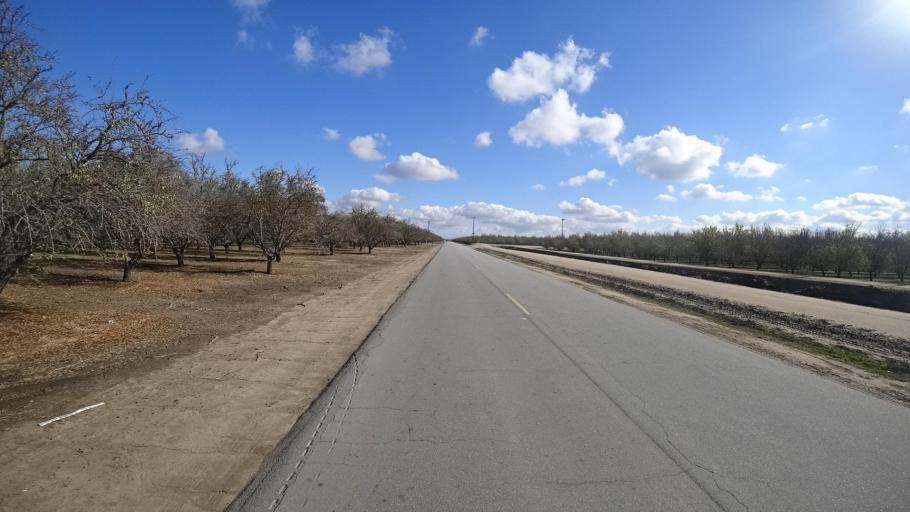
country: US
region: California
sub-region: Kern County
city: McFarland
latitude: 35.6742
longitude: -119.3050
